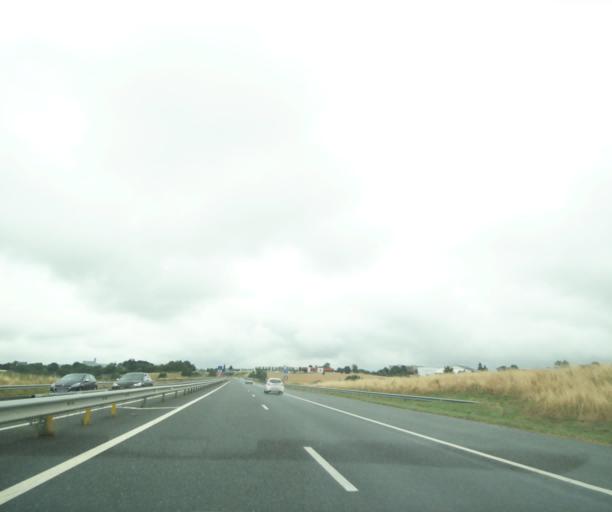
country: FR
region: Midi-Pyrenees
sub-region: Departement de l'Aveyron
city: Luc-la-Primaube
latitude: 44.3218
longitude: 2.5518
